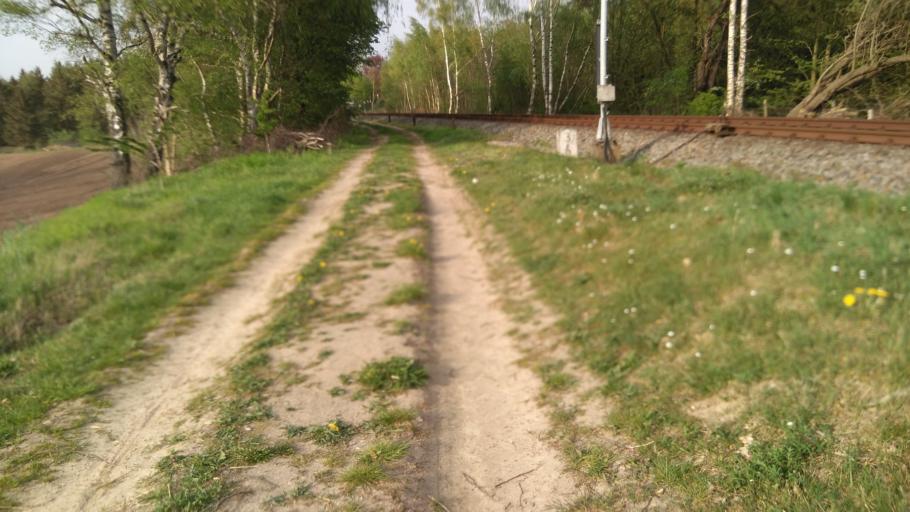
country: DE
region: Lower Saxony
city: Buxtehude
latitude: 53.4572
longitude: 9.6521
